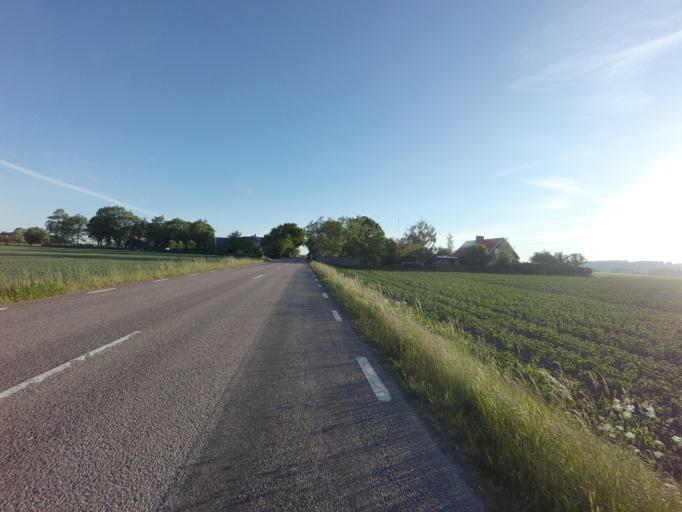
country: SE
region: Skane
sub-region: Helsingborg
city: Odakra
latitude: 56.1578
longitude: 12.6787
